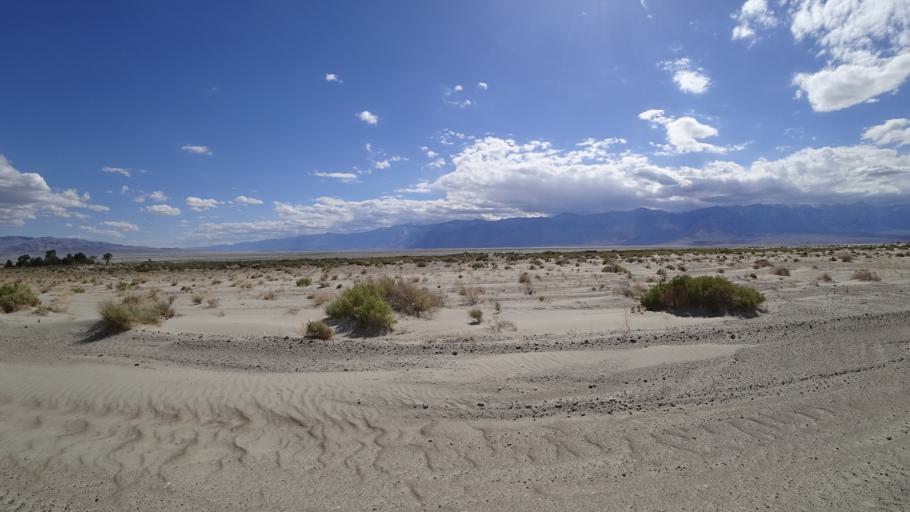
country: US
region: California
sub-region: Inyo County
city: Lone Pine
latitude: 36.4961
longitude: -117.8781
